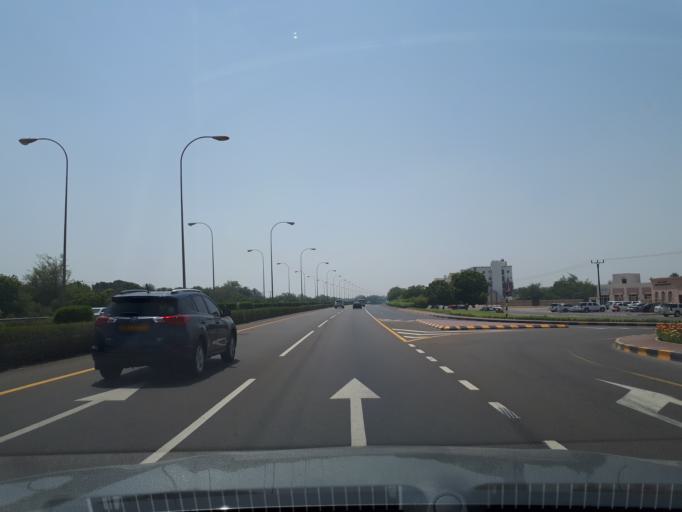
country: OM
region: Al Batinah
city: Al Sohar
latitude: 24.3967
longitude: 56.6730
